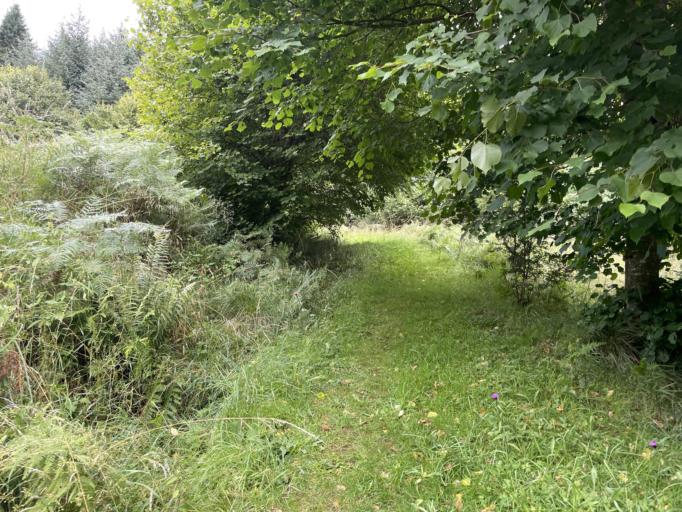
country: GB
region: Scotland
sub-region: South Ayrshire
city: Maybole
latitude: 55.2054
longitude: -4.6721
